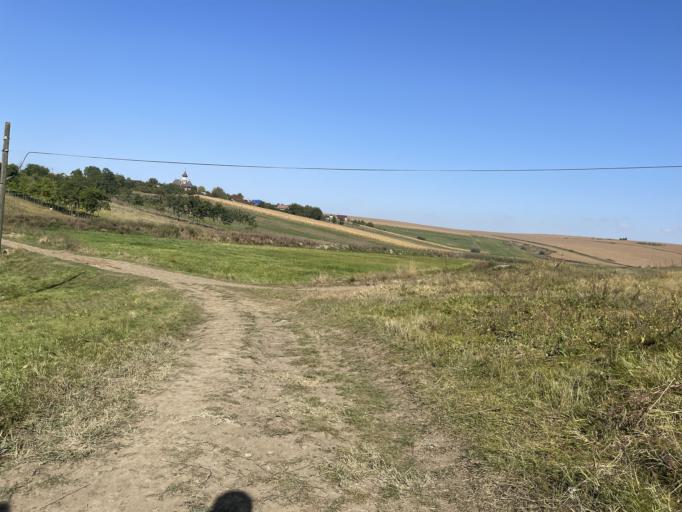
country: RO
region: Iasi
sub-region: Comuna Dumesti
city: Pausesti
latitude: 47.1612
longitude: 27.3118
